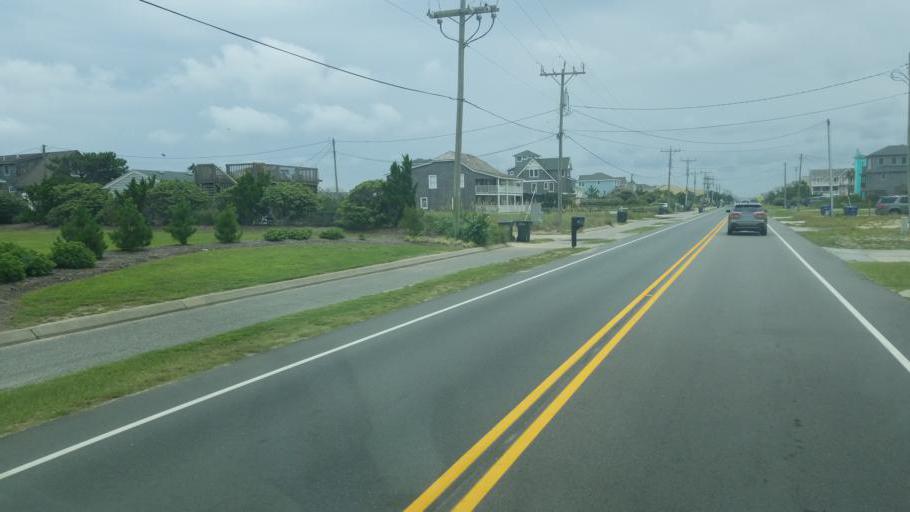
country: US
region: North Carolina
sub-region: Dare County
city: Nags Head
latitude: 35.9444
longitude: -75.6169
